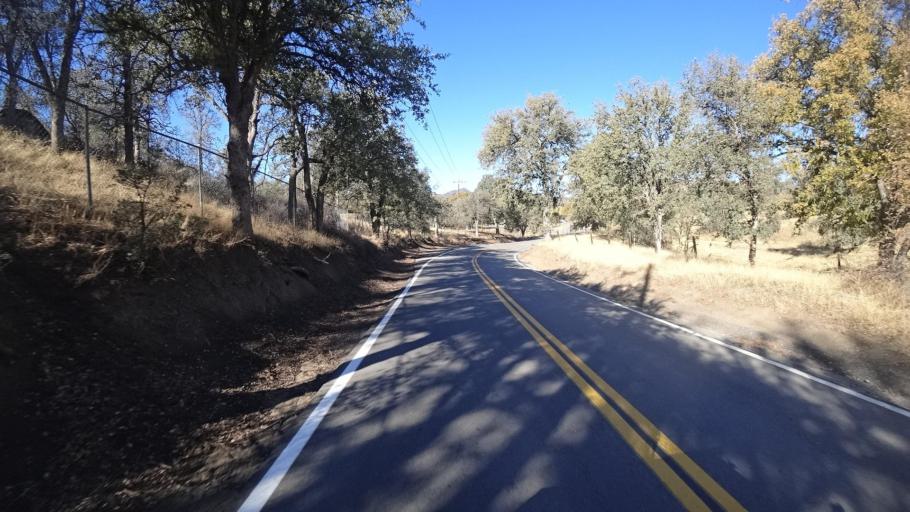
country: US
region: California
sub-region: Kern County
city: Alta Sierra
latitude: 35.7224
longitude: -118.6958
